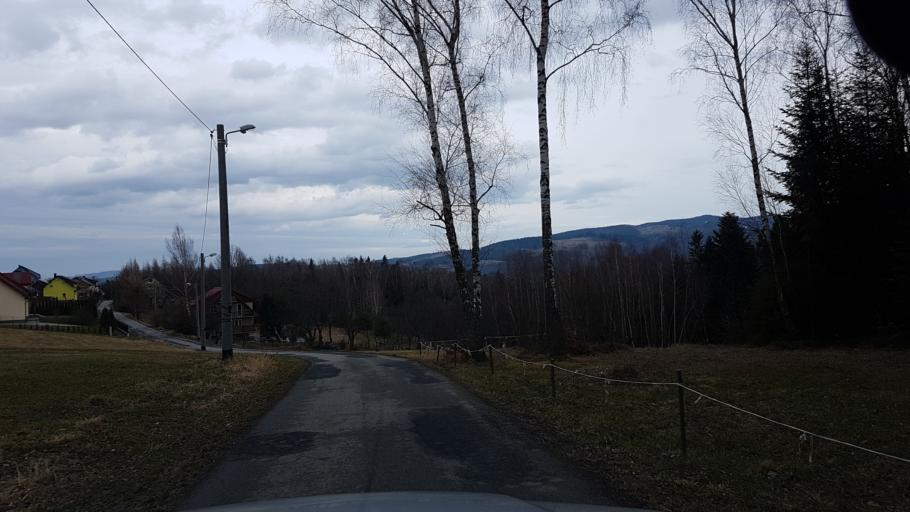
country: PL
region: Lesser Poland Voivodeship
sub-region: Powiat nowosadecki
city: Stary Sacz
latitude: 49.5286
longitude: 20.6251
